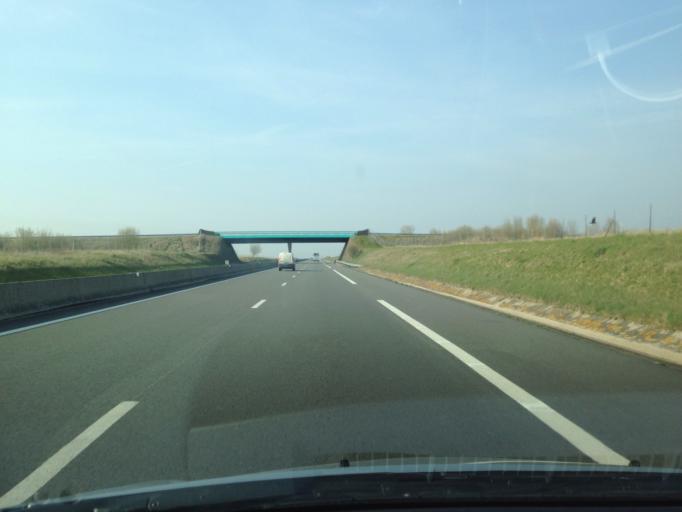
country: FR
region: Picardie
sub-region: Departement de la Somme
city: Rue
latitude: 50.3071
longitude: 1.7244
